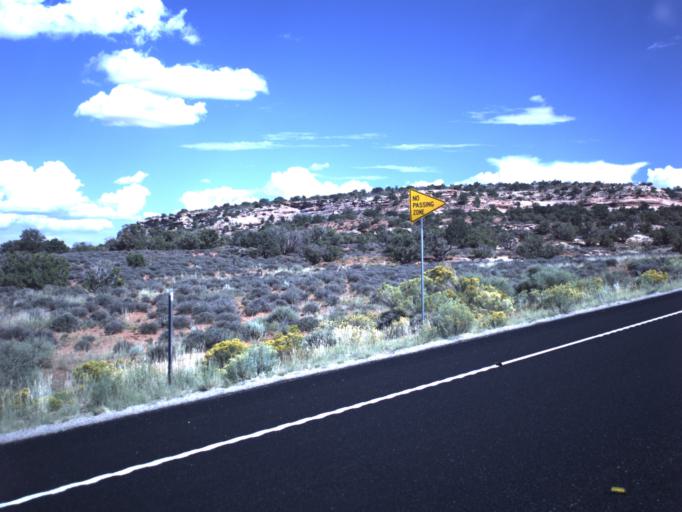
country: US
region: Utah
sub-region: Grand County
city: Moab
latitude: 38.5828
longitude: -109.8004
